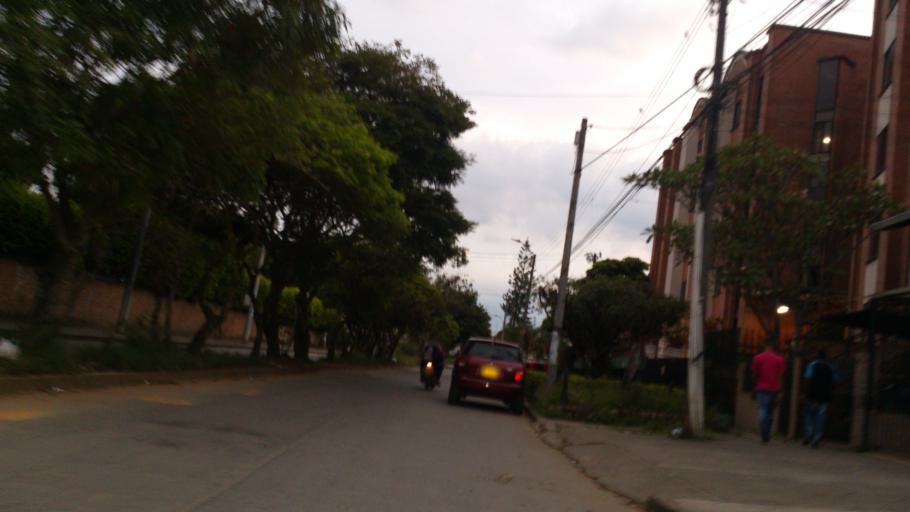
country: CO
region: Valle del Cauca
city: Jamundi
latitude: 3.2632
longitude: -76.5350
